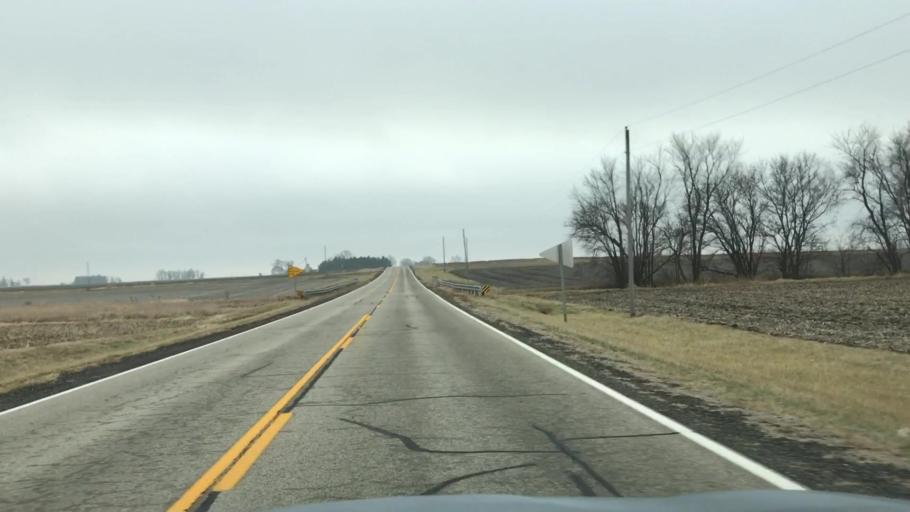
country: US
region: Illinois
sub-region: McLean County
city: Hudson
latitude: 40.6224
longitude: -88.9456
